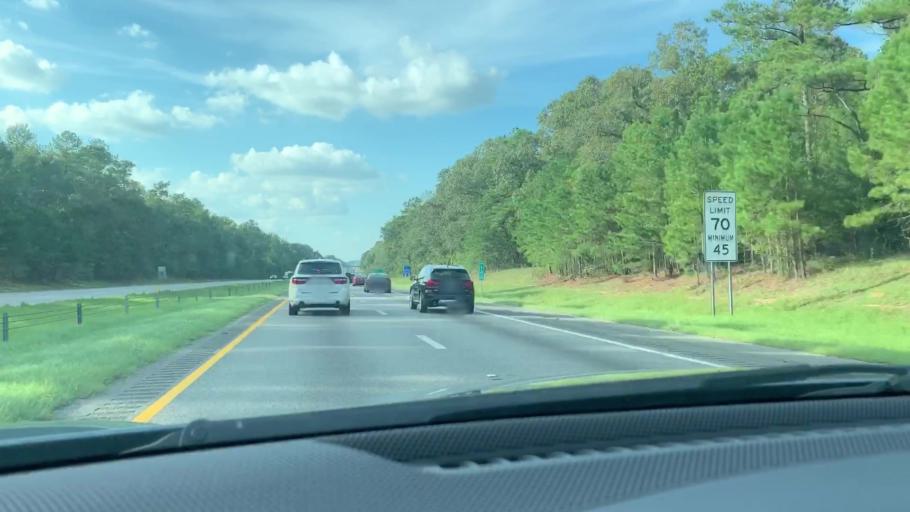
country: US
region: South Carolina
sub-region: Orangeburg County
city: Brookdale
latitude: 33.5270
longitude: -80.7979
